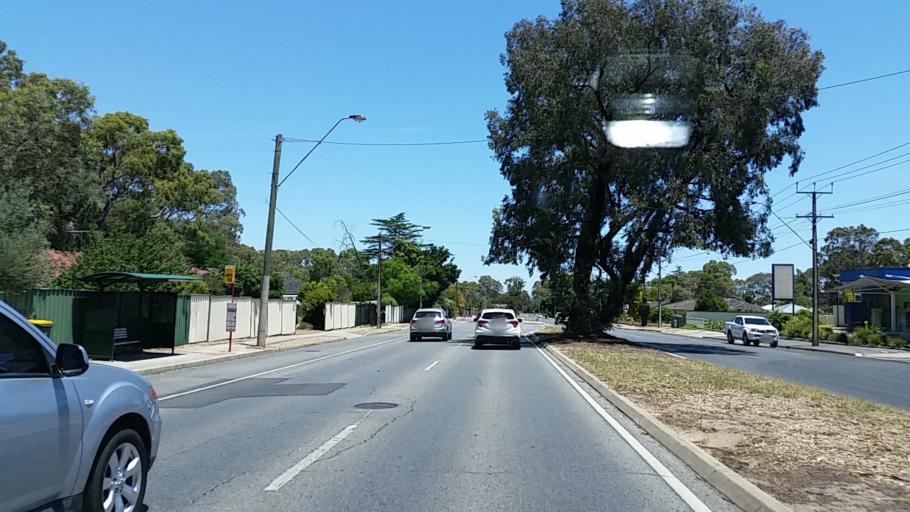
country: AU
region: South Australia
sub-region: Tea Tree Gully
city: Hope Valley
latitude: -34.8235
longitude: 138.7103
